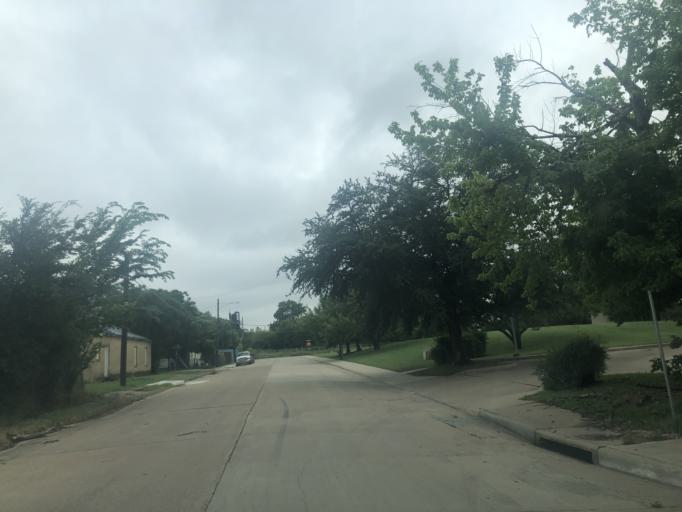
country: US
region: Texas
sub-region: Dallas County
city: Cockrell Hill
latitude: 32.7769
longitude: -96.8593
